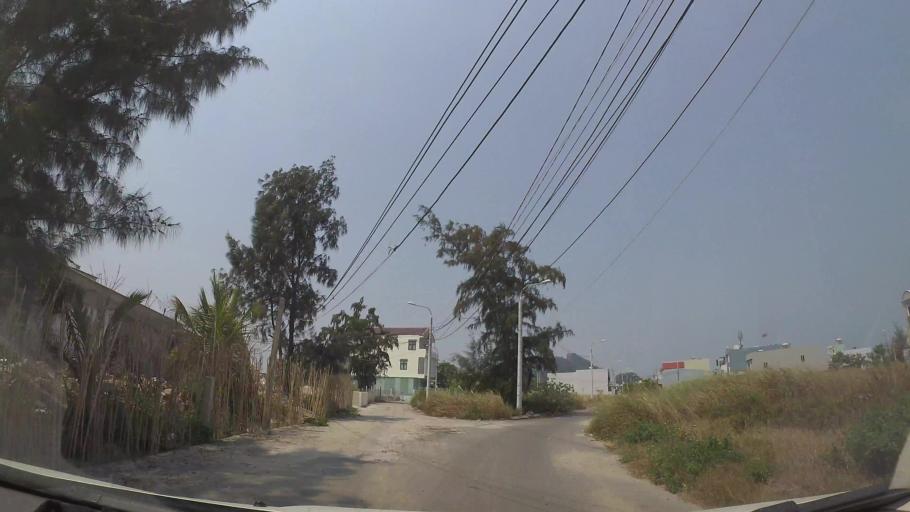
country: VN
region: Da Nang
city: Ngu Hanh Son
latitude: 15.9961
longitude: 108.2656
